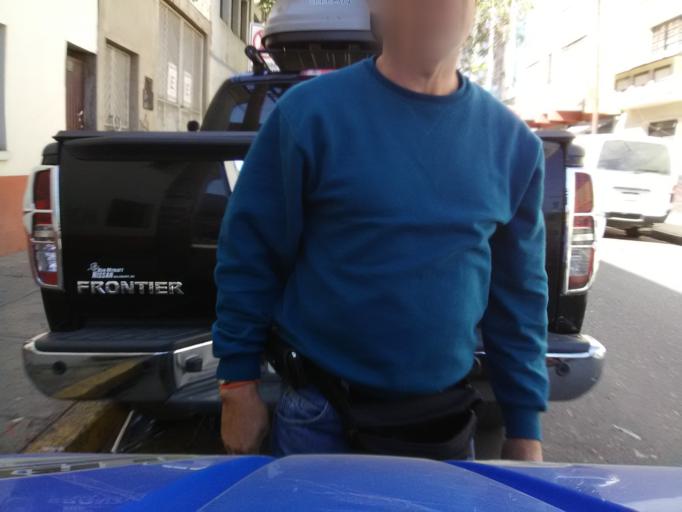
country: BO
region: Cochabamba
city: Cochabamba
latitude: -17.3976
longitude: -66.1498
